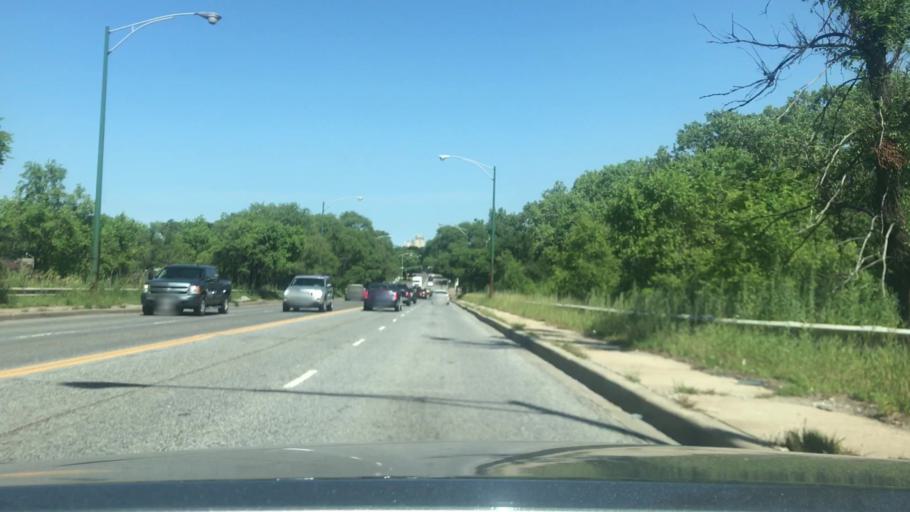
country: US
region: Illinois
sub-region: Cook County
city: Burnham
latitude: 41.7080
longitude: -87.5714
